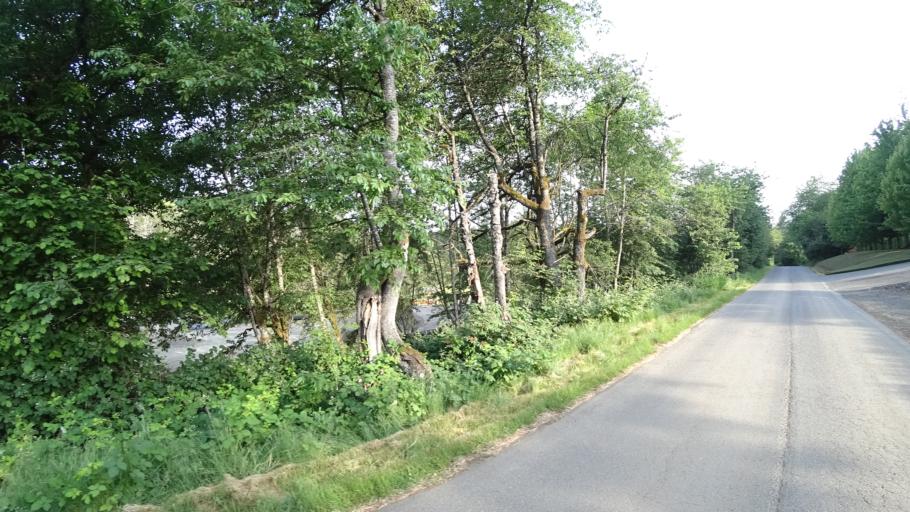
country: US
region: Oregon
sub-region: Clackamas County
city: Happy Valley
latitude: 45.4474
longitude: -122.5019
